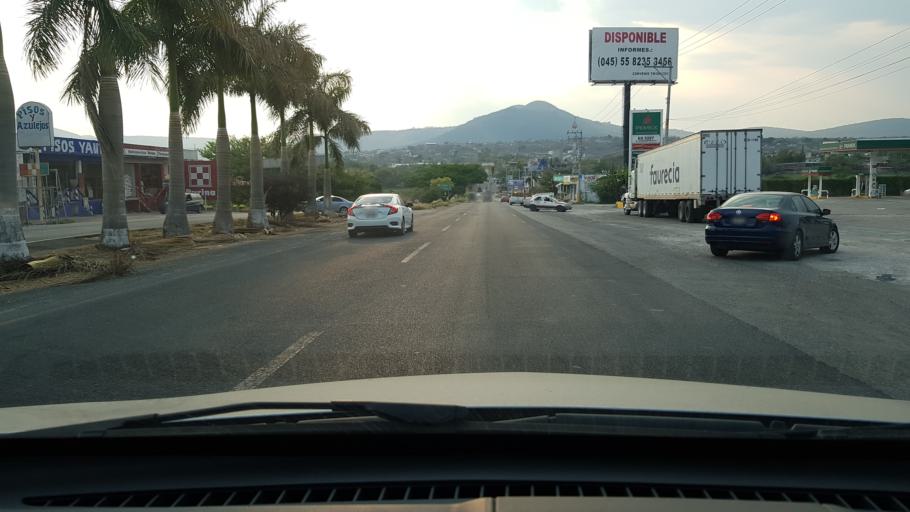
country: MX
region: Morelos
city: Yautepec
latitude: 18.8706
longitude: -99.0684
